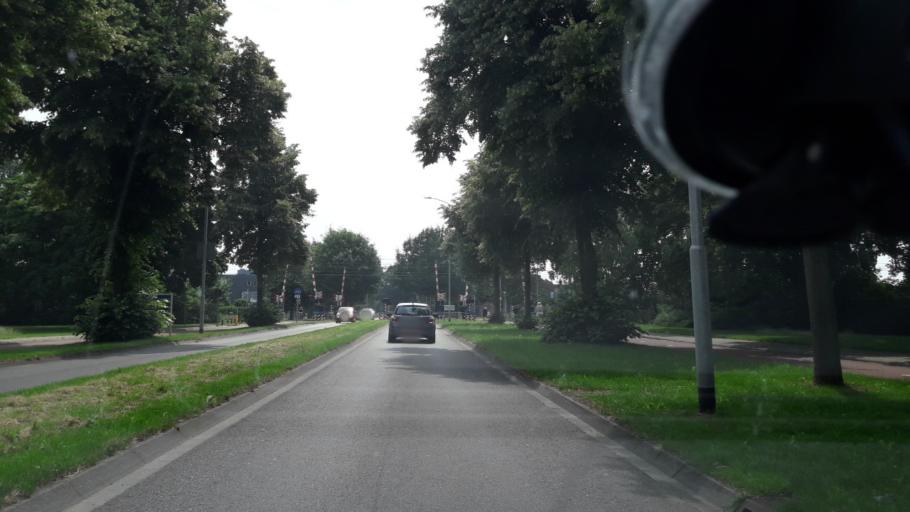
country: NL
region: Gelderland
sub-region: Gemeente Harderwijk
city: Harderwijk
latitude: 52.3404
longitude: 5.6310
